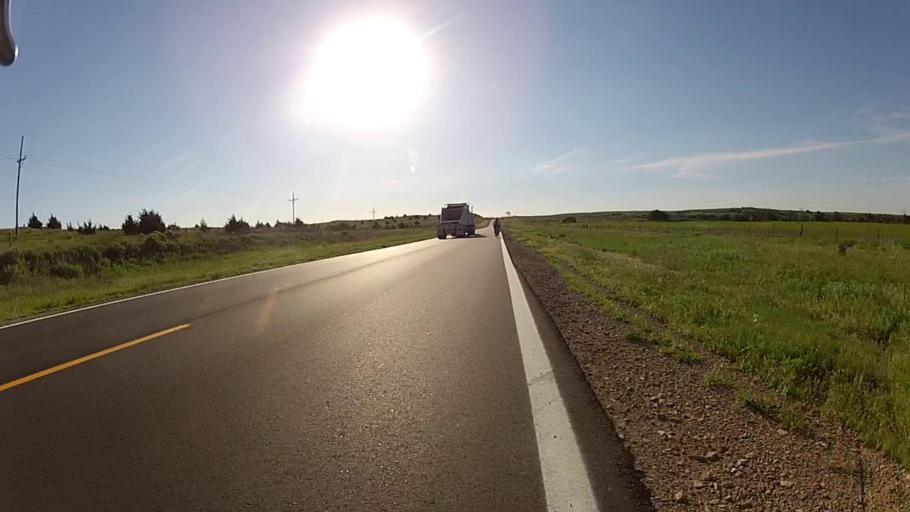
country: US
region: Kansas
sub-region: Comanche County
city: Coldwater
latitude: 37.2811
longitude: -99.0422
